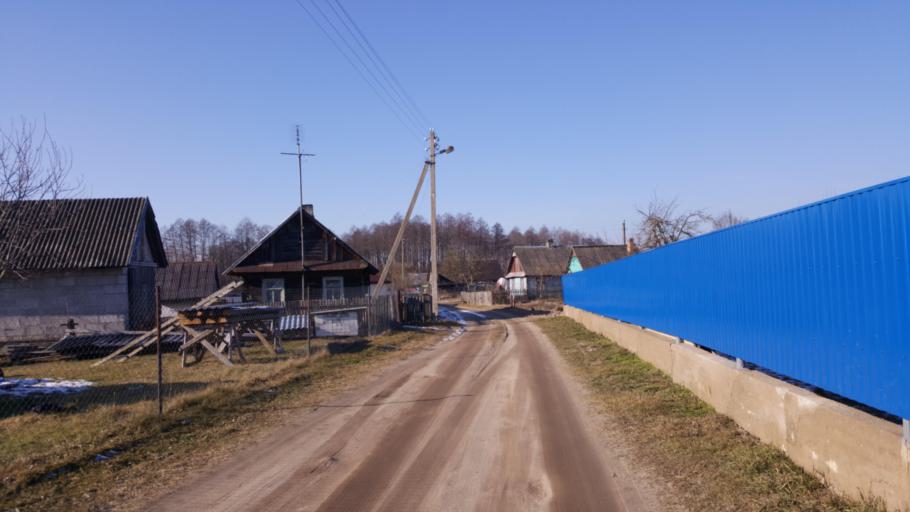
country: BY
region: Brest
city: Kamyanyets
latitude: 52.3859
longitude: 23.7962
